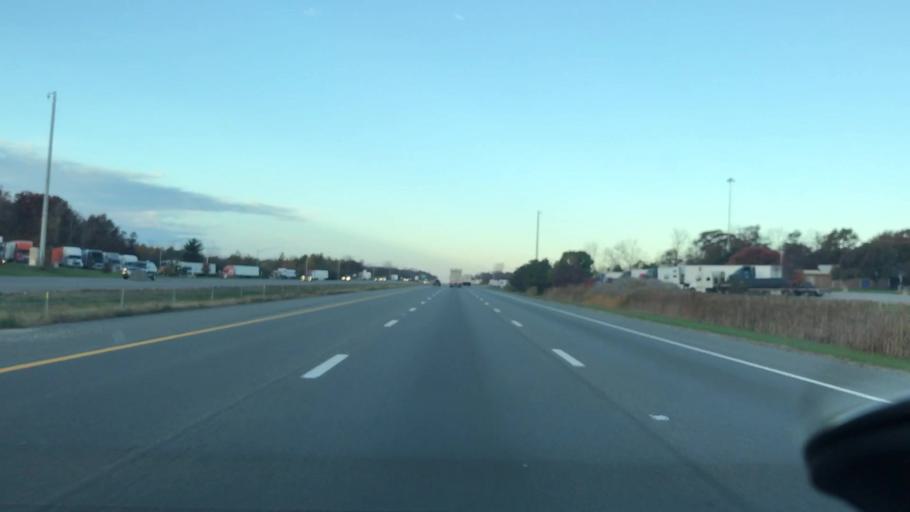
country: US
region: Ohio
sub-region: Madison County
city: Choctaw Lake
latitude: 39.9411
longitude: -83.5309
